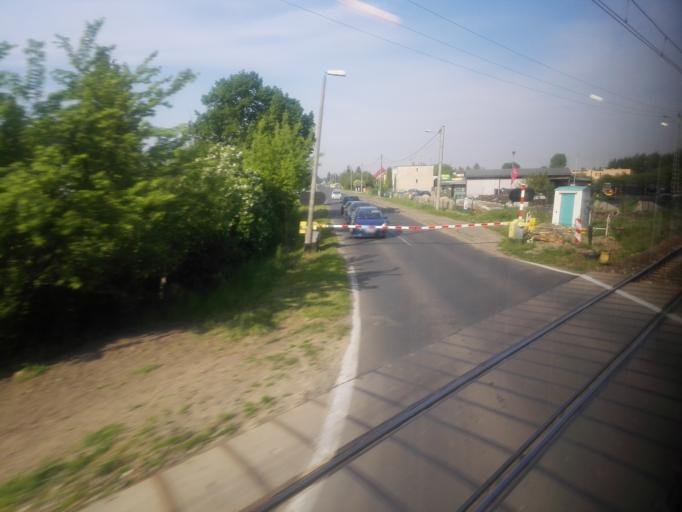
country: PL
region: Greater Poland Voivodeship
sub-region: Powiat wrzesinski
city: Wrzesnia
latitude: 52.3362
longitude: 17.5997
